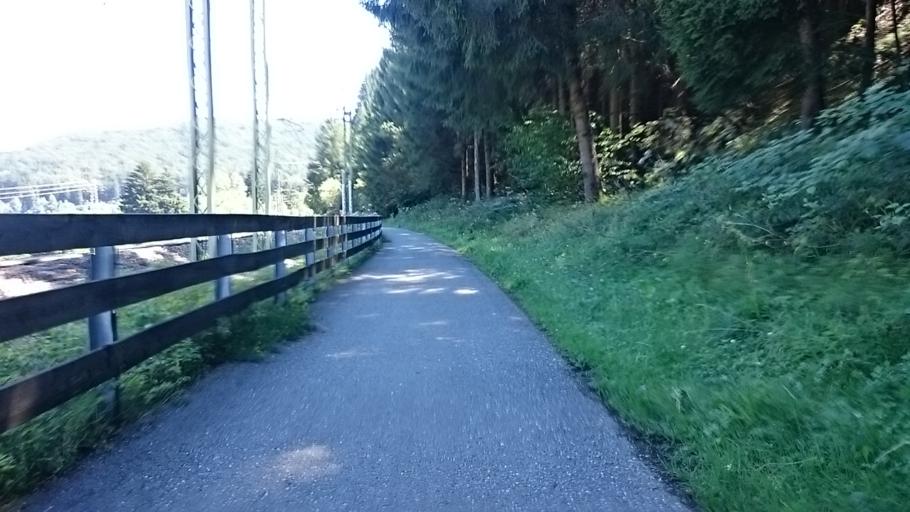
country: IT
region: Trentino-Alto Adige
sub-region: Bolzano
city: Chienes
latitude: 46.7861
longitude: 11.8644
